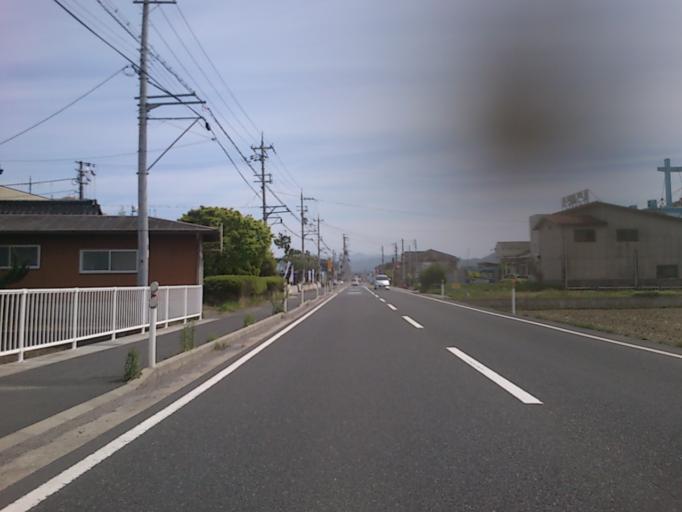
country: JP
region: Kyoto
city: Miyazu
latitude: 35.6268
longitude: 135.0724
